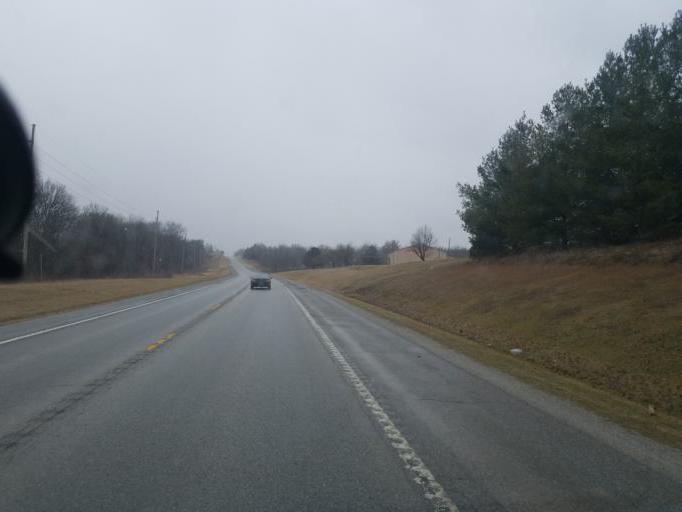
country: US
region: Missouri
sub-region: Schuyler County
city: Lancaster
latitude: 40.3622
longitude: -92.5632
